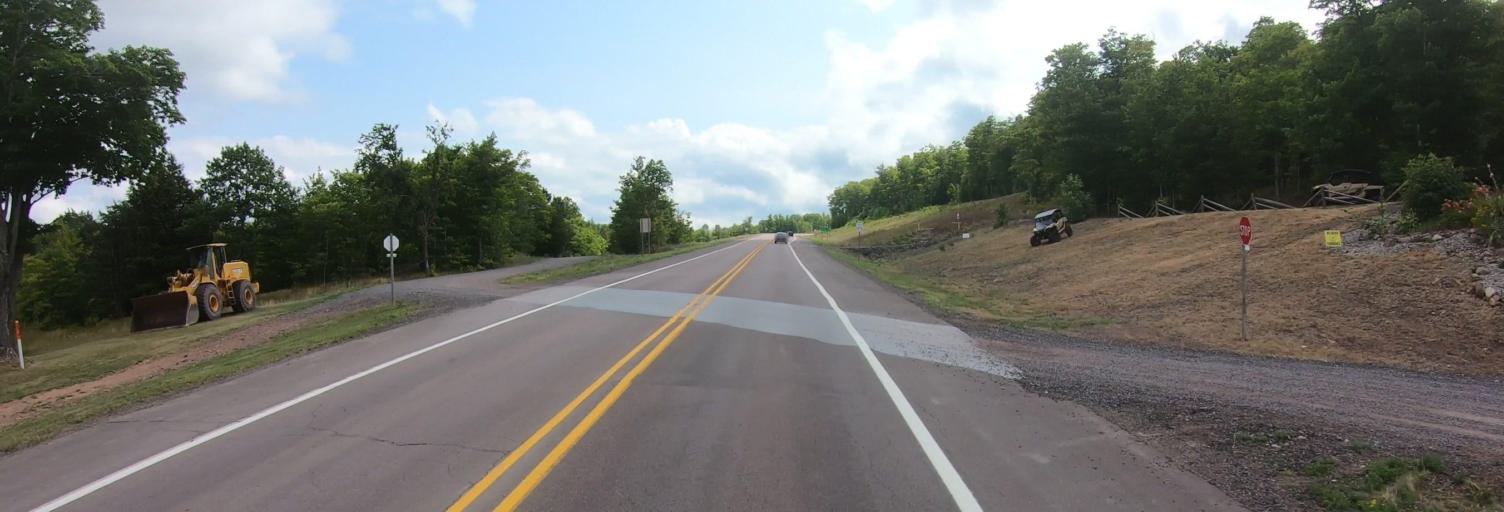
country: US
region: Michigan
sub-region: Houghton County
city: Hancock
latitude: 47.0671
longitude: -88.6406
